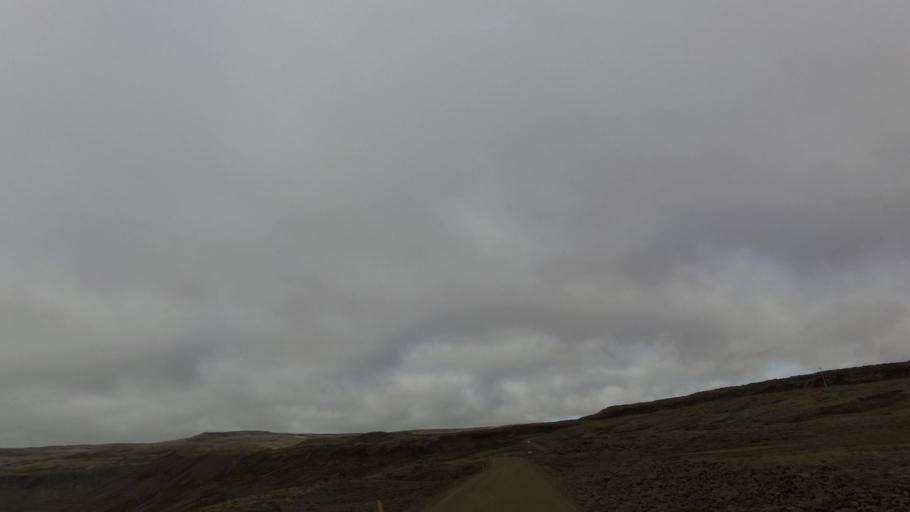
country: IS
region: West
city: Olafsvik
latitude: 65.5435
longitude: -24.3490
